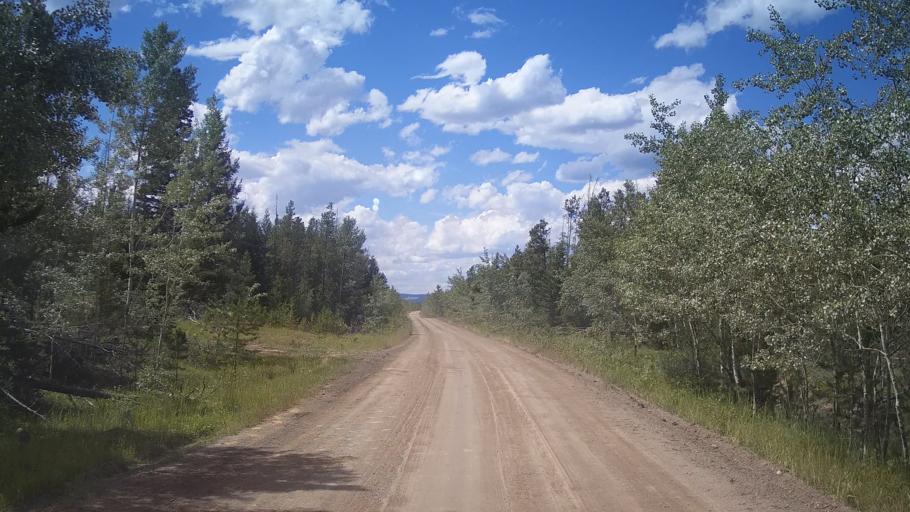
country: CA
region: British Columbia
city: Lillooet
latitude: 51.3386
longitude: -121.9129
